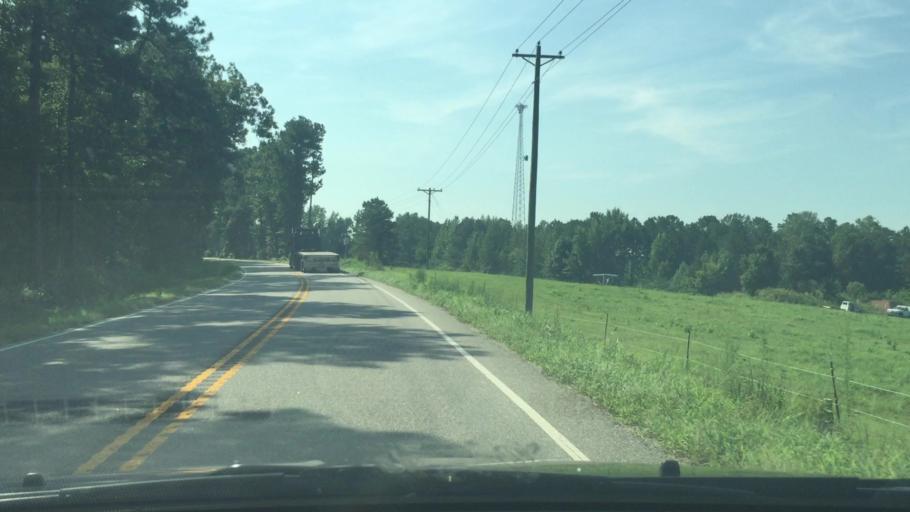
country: US
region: Virginia
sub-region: Sussex County
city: Sussex
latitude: 37.0372
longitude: -77.3082
